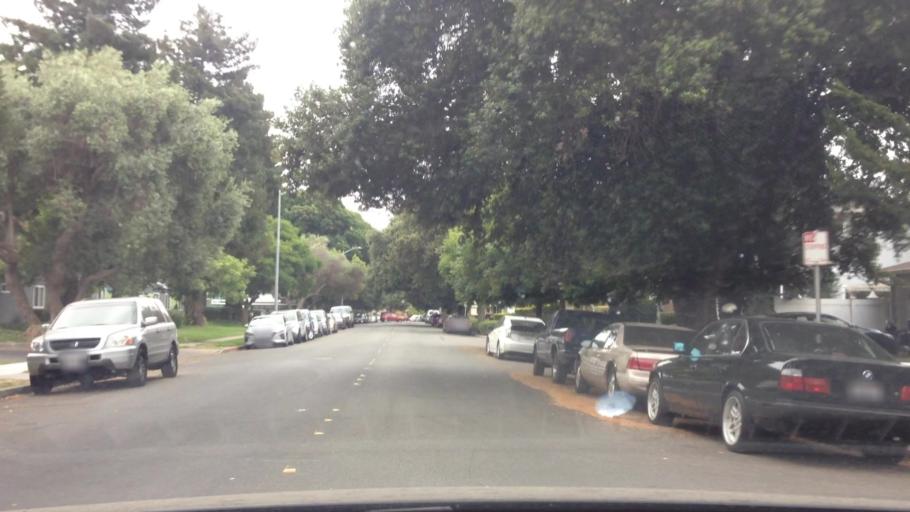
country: US
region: California
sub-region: Alameda County
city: Fremont
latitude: 37.5599
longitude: -121.9964
